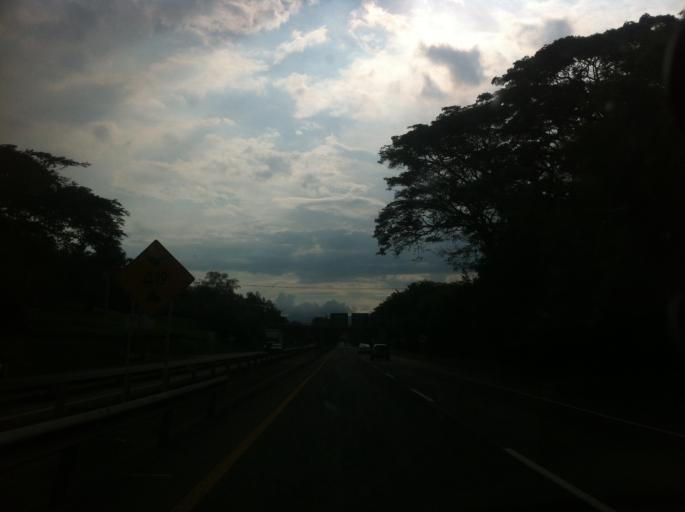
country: CO
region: Valle del Cauca
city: San Pedro
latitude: 3.9789
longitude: -76.2434
